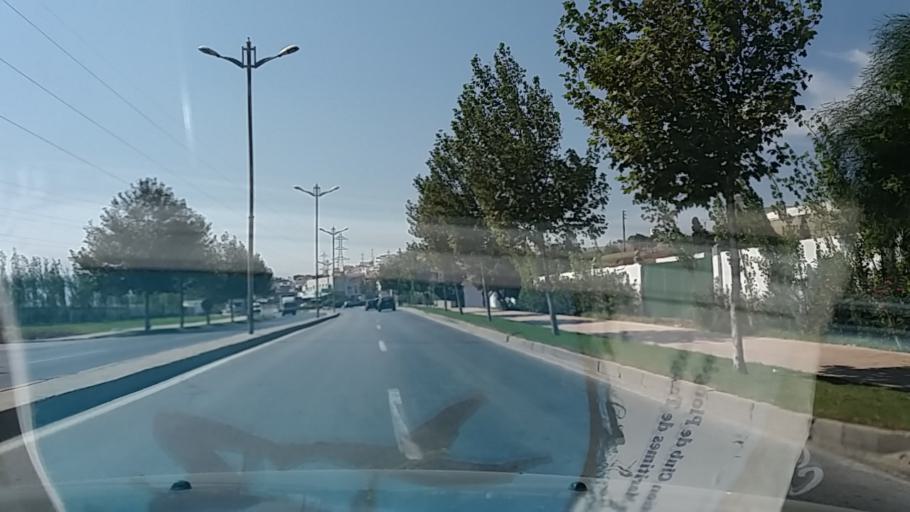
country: MA
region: Tanger-Tetouan
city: Tetouan
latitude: 35.5651
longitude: -5.4199
